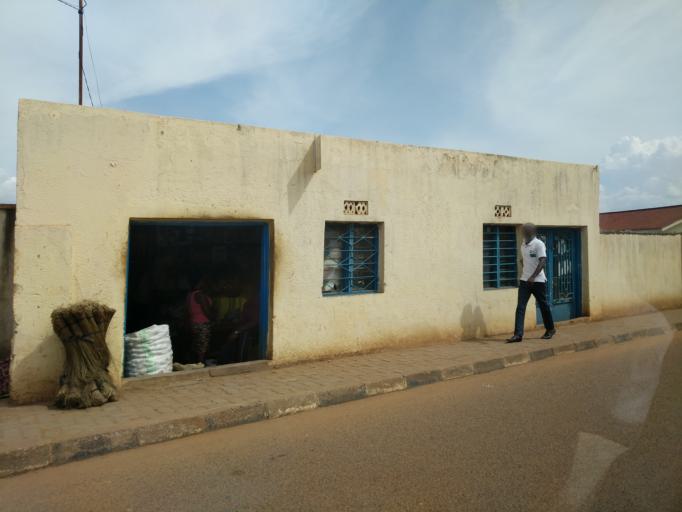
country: RW
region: Kigali
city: Kigali
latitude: -1.9818
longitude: 30.1329
